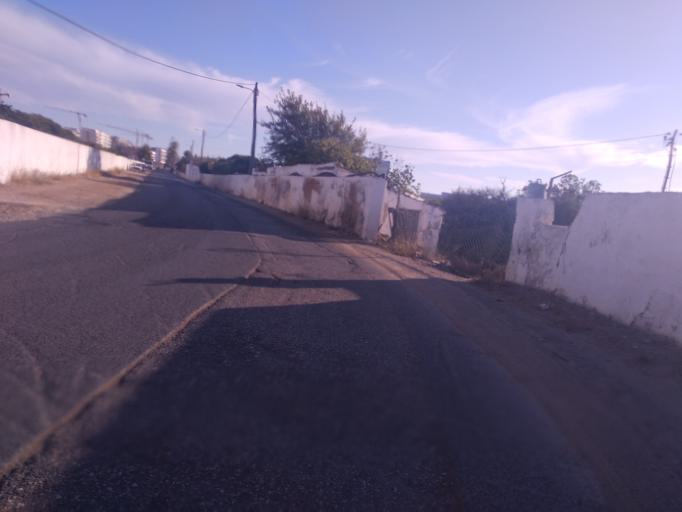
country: PT
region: Faro
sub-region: Faro
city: Faro
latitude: 37.0378
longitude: -7.9404
